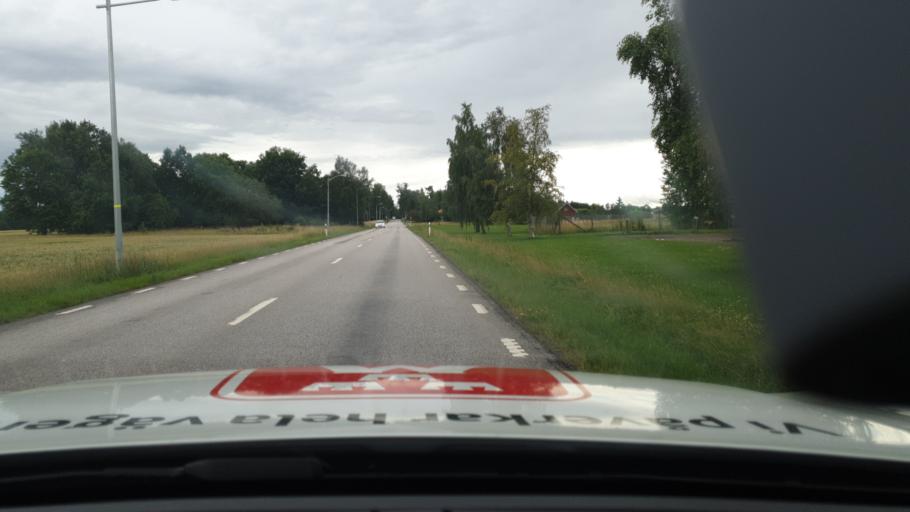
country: SE
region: Vaestra Goetaland
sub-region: Skovde Kommun
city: Stopen
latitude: 58.5657
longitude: 14.0092
